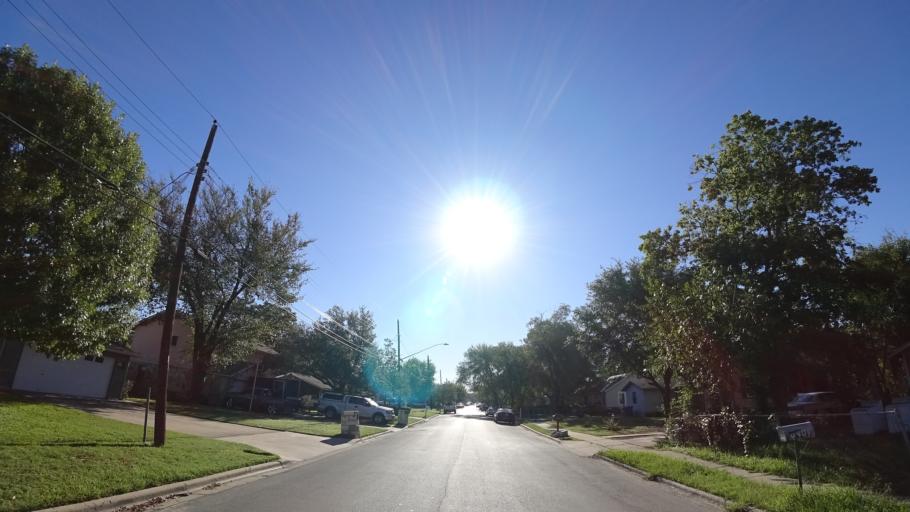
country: US
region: Texas
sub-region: Travis County
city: Austin
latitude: 30.2283
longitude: -97.7001
